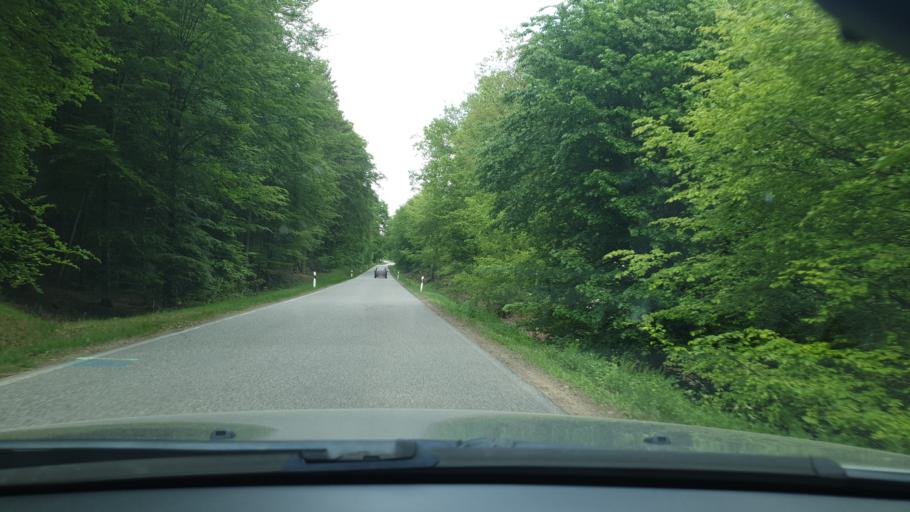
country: DE
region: Rheinland-Pfalz
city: Oberarnbach
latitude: 49.3861
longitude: 7.5635
